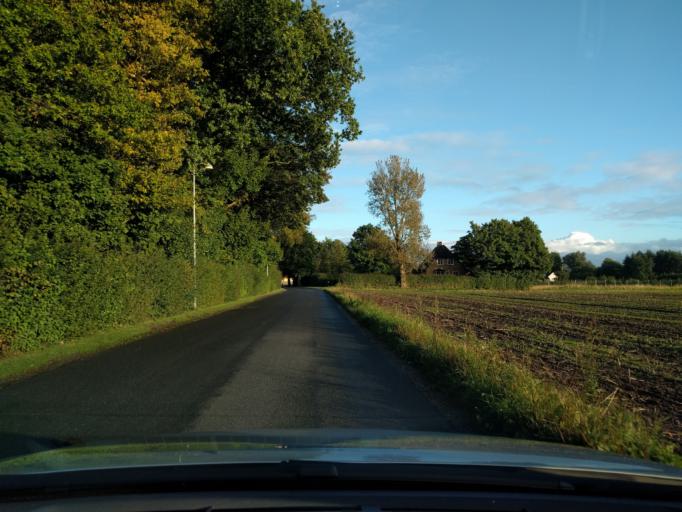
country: DK
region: South Denmark
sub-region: Odense Kommune
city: Bullerup
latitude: 55.4283
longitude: 10.4900
